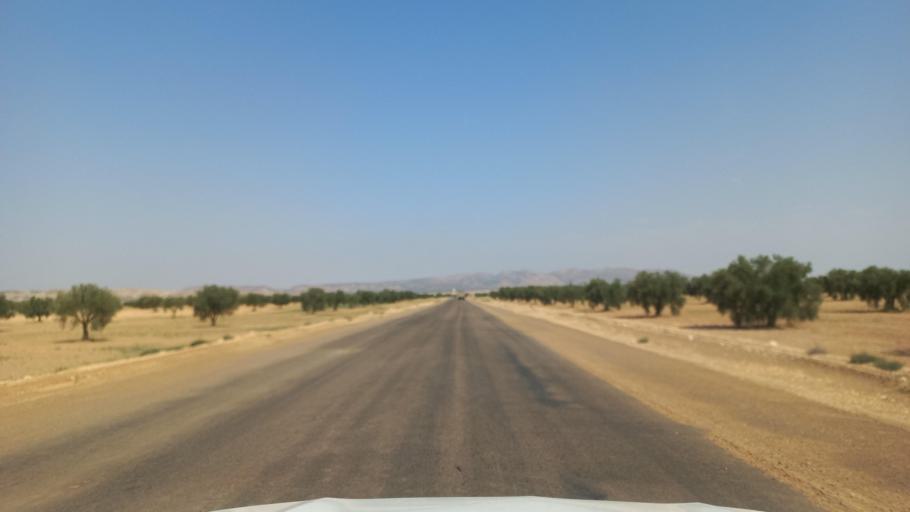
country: TN
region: Al Qasrayn
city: Sbiba
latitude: 35.3412
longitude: 9.0567
